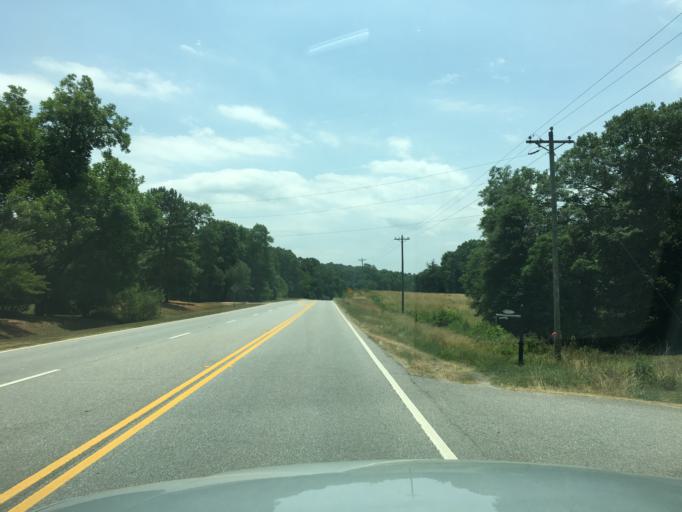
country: US
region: Georgia
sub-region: Hart County
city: Royston
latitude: 34.2589
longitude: -83.1693
